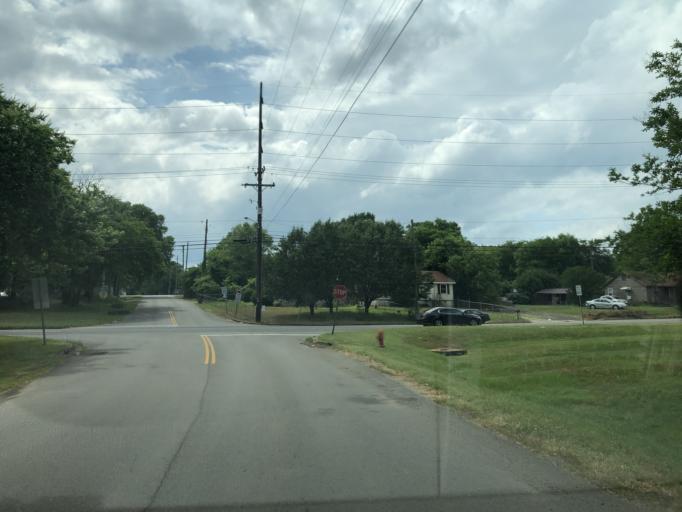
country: US
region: Tennessee
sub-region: Davidson County
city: Goodlettsville
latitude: 36.2693
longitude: -86.6894
